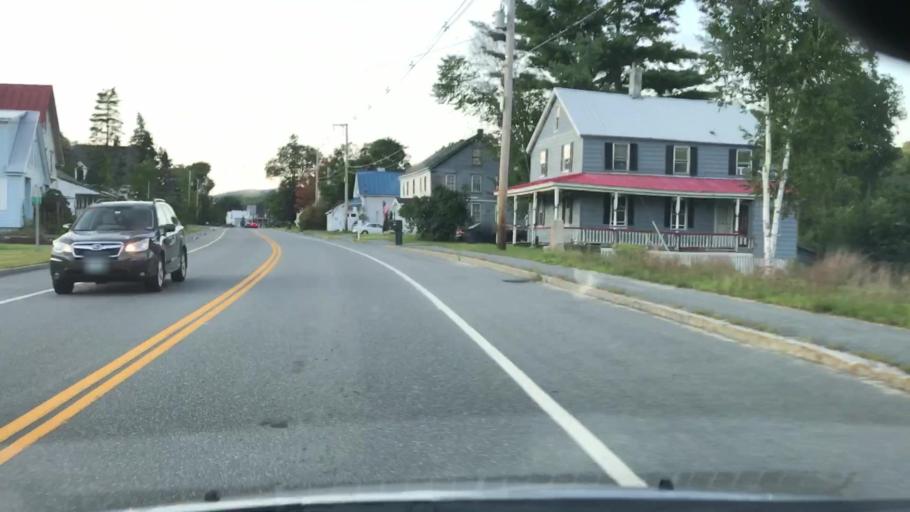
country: US
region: New Hampshire
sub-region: Grafton County
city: Rumney
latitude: 43.9154
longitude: -71.8880
